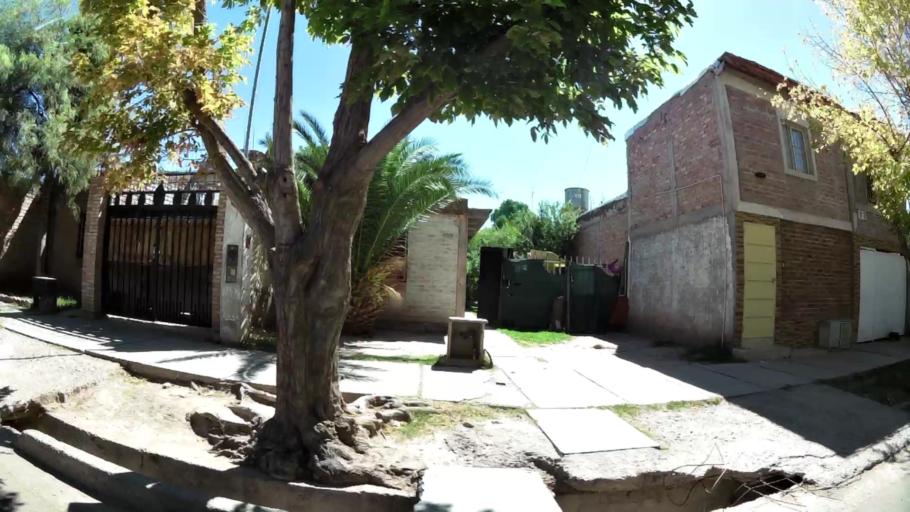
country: AR
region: Mendoza
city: Las Heras
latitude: -32.8335
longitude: -68.8449
